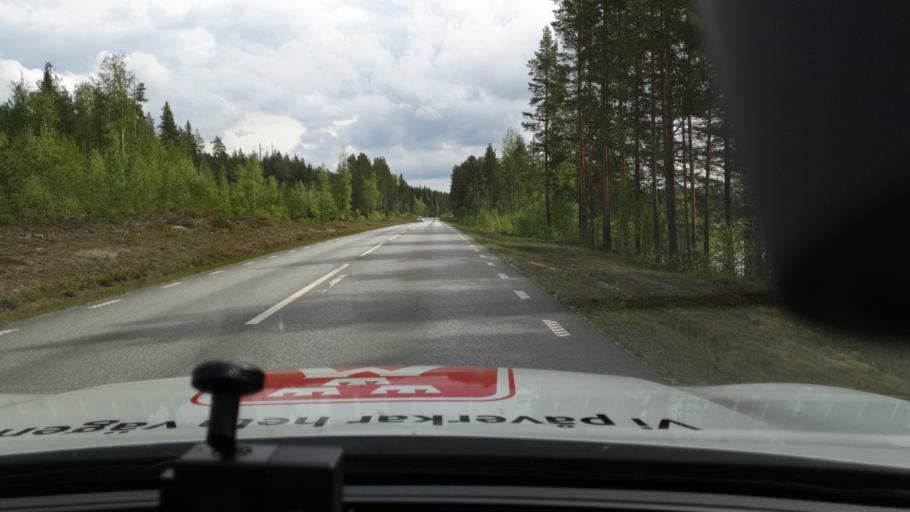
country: SE
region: Vaesterbotten
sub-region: Lycksele Kommun
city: Lycksele
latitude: 64.5481
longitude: 18.7400
